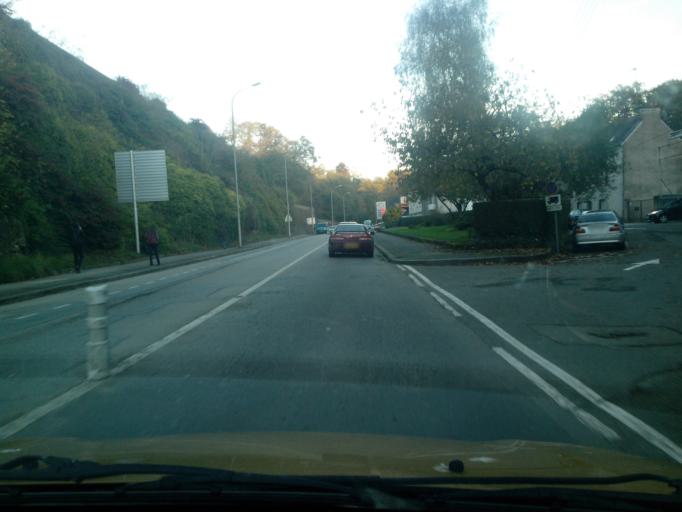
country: FR
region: Brittany
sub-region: Departement du Morbihan
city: Hennebont
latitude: 47.8043
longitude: -3.2728
